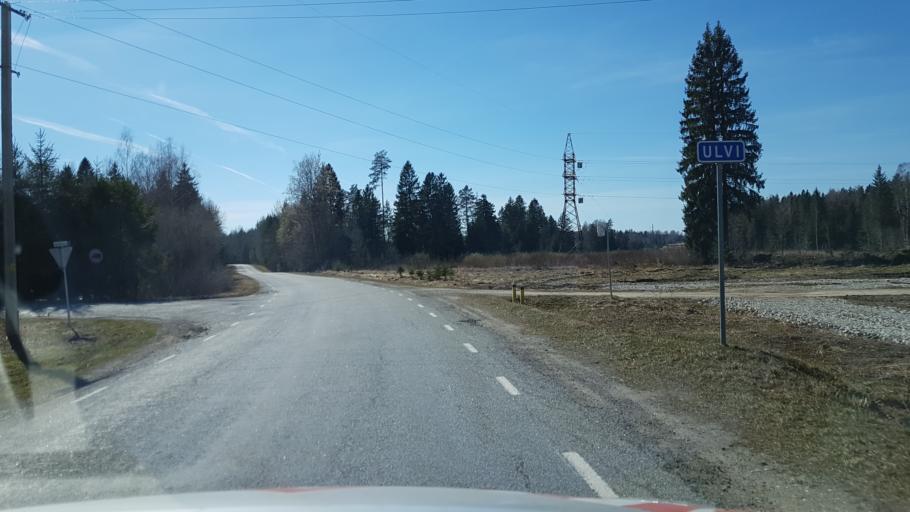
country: EE
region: Laeaene-Virumaa
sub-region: Viru-Nigula vald
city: Kunda
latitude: 59.3333
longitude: 26.6340
